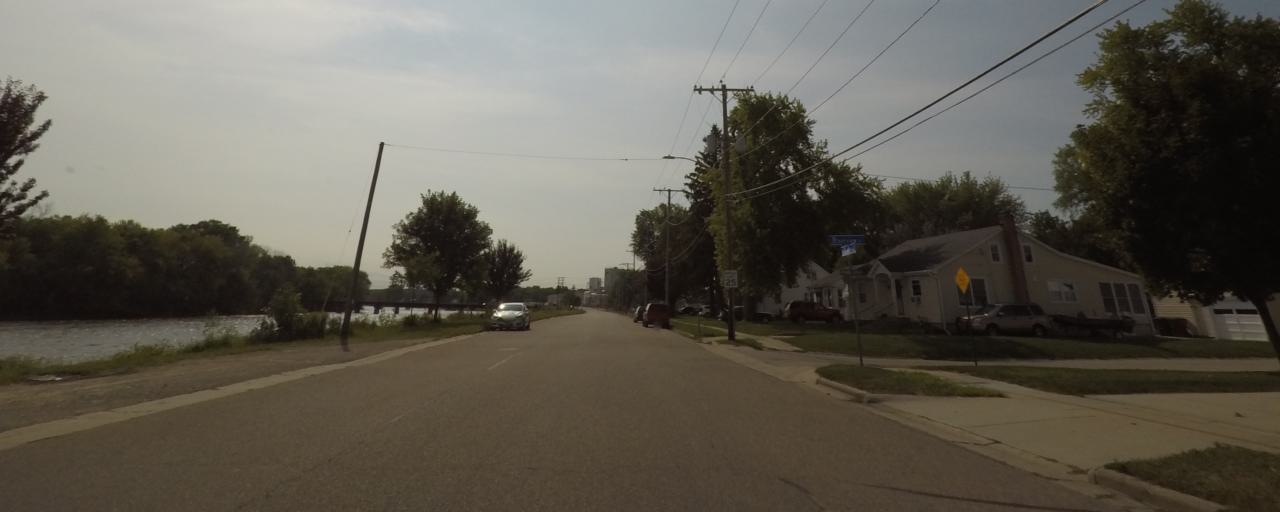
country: US
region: Wisconsin
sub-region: Jefferson County
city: Jefferson
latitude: 43.0002
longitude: -88.8123
